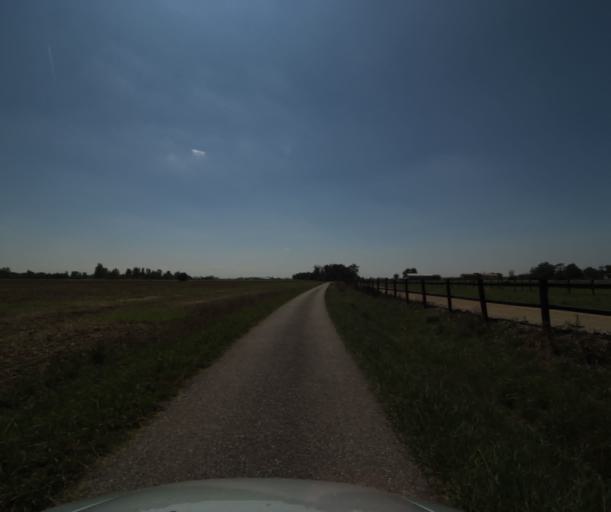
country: FR
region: Midi-Pyrenees
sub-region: Departement de la Haute-Garonne
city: Labastidette
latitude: 43.4588
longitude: 1.2669
